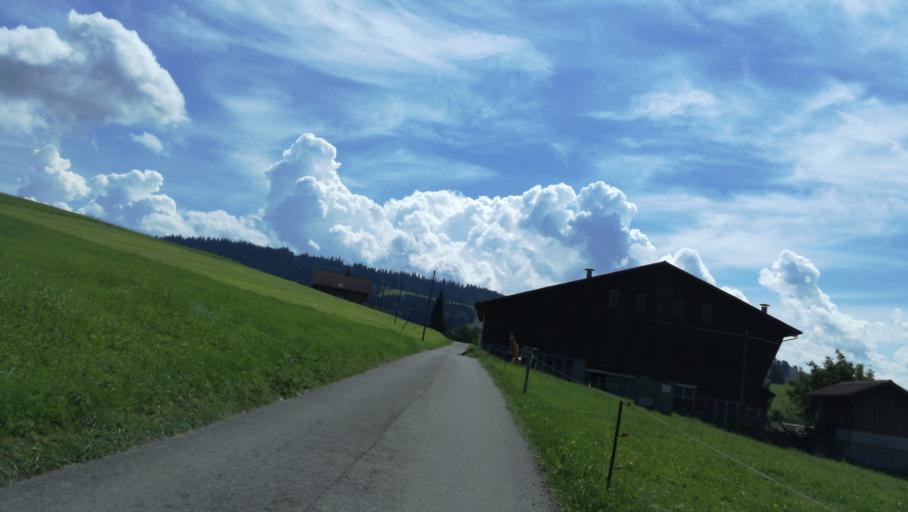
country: CH
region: Schwyz
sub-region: Bezirk Schwyz
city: Rothenthurm
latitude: 47.1395
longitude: 8.6384
